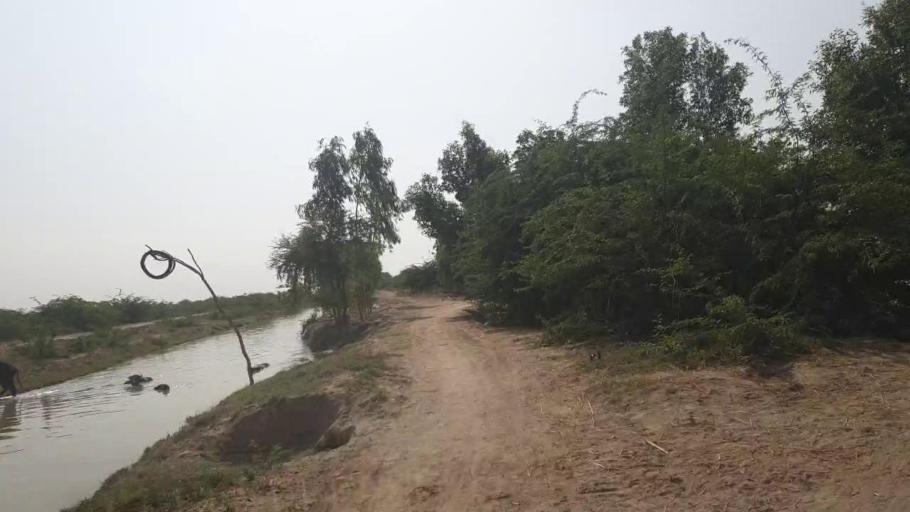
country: PK
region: Sindh
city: Kadhan
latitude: 24.5046
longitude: 68.8500
